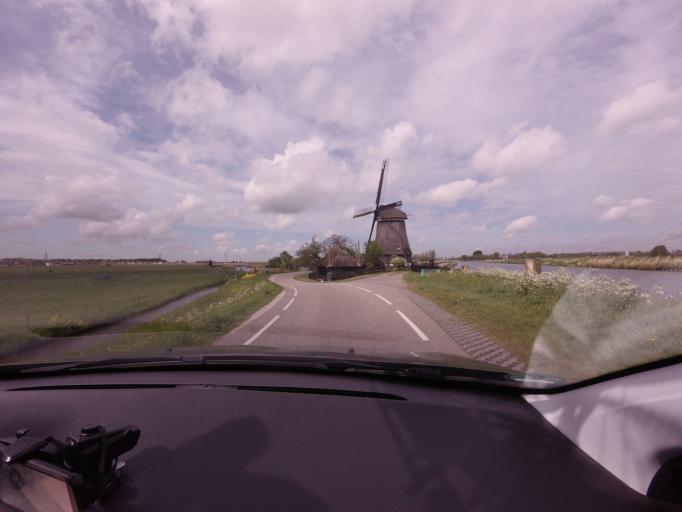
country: NL
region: North Holland
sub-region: Gemeente Beemster
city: Halfweg
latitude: 52.5116
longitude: 4.9206
